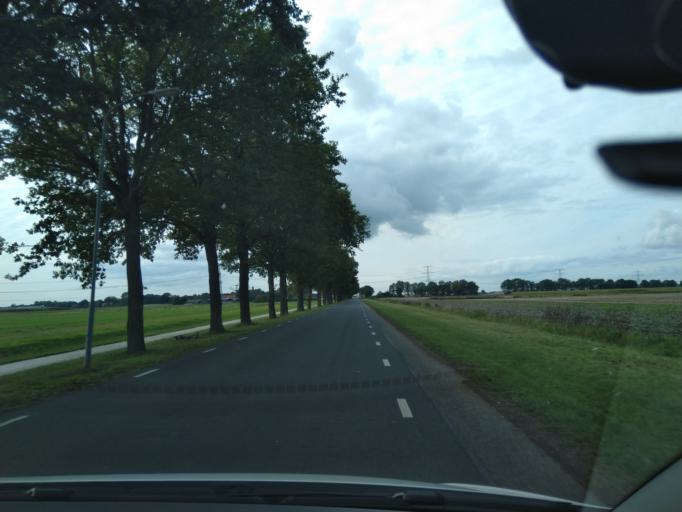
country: NL
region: Groningen
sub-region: Gemeente Pekela
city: Oude Pekela
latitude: 53.0915
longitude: 6.9657
